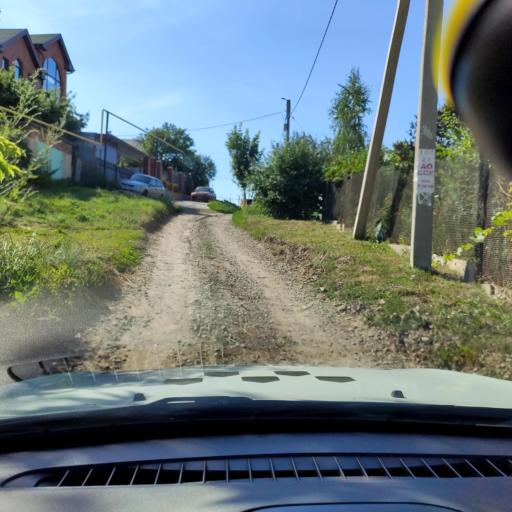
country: RU
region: Samara
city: Zhigulevsk
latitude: 53.3973
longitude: 49.5288
